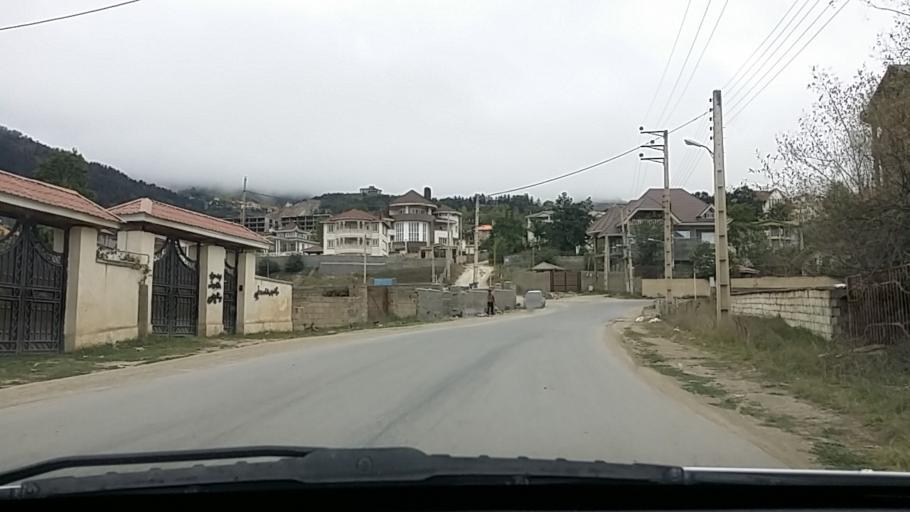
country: IR
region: Mazandaran
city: `Abbasabad
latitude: 36.4987
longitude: 51.1563
